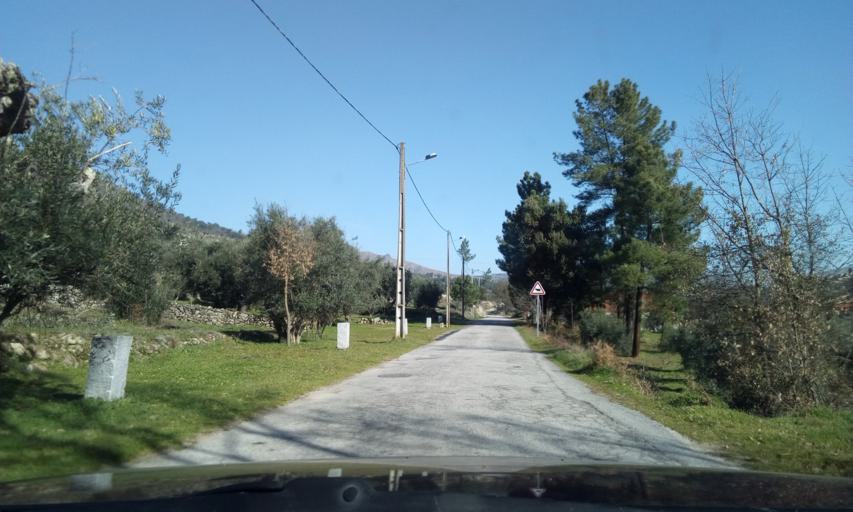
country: PT
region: Guarda
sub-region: Celorico da Beira
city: Celorico da Beira
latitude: 40.6815
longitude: -7.4554
